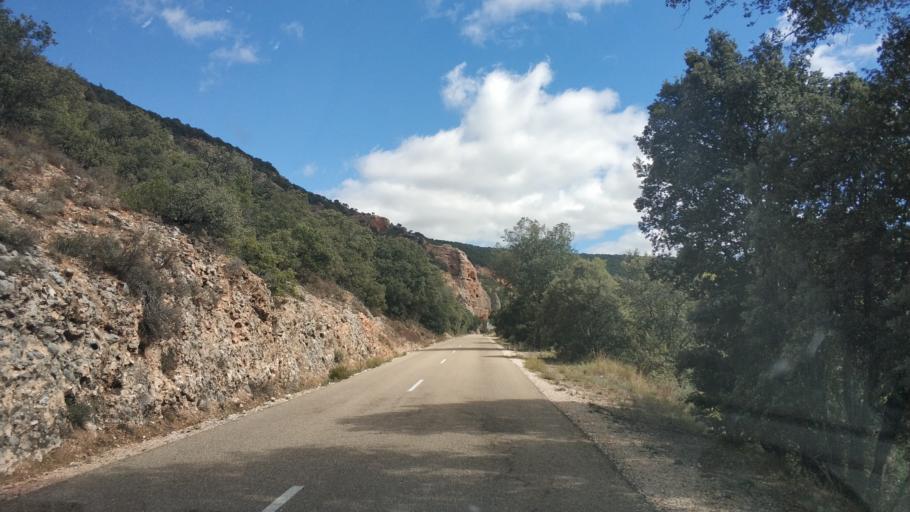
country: ES
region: Castille and Leon
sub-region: Provincia de Burgos
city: Covarrubias
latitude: 42.0525
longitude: -3.4999
